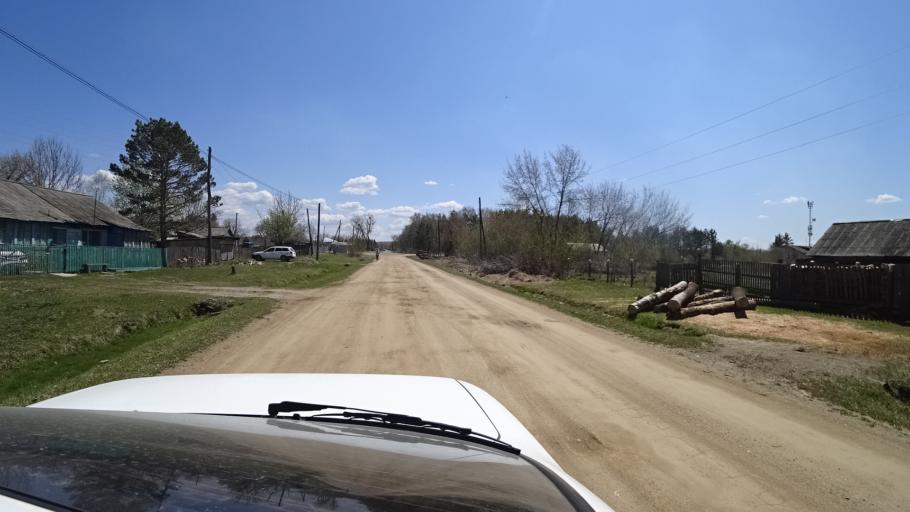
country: RU
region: Primorskiy
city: Dal'nerechensk
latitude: 45.7977
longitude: 133.7671
